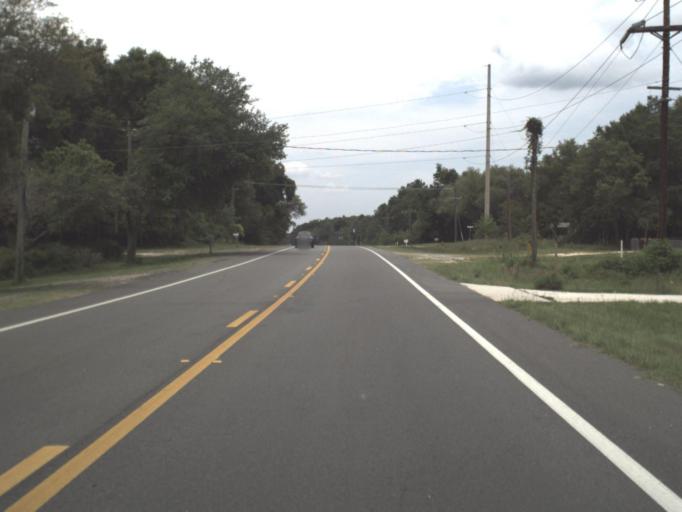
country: US
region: Florida
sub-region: Putnam County
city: Interlachen
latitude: 29.6134
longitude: -81.9843
